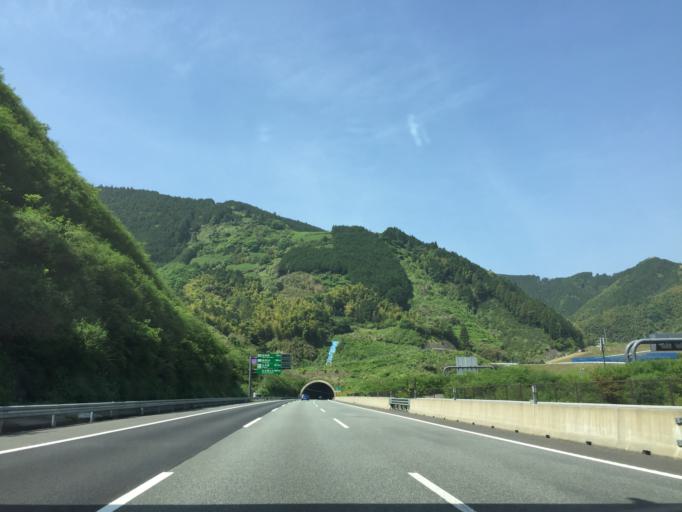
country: JP
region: Shizuoka
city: Shizuoka-shi
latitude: 35.0658
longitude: 138.4496
